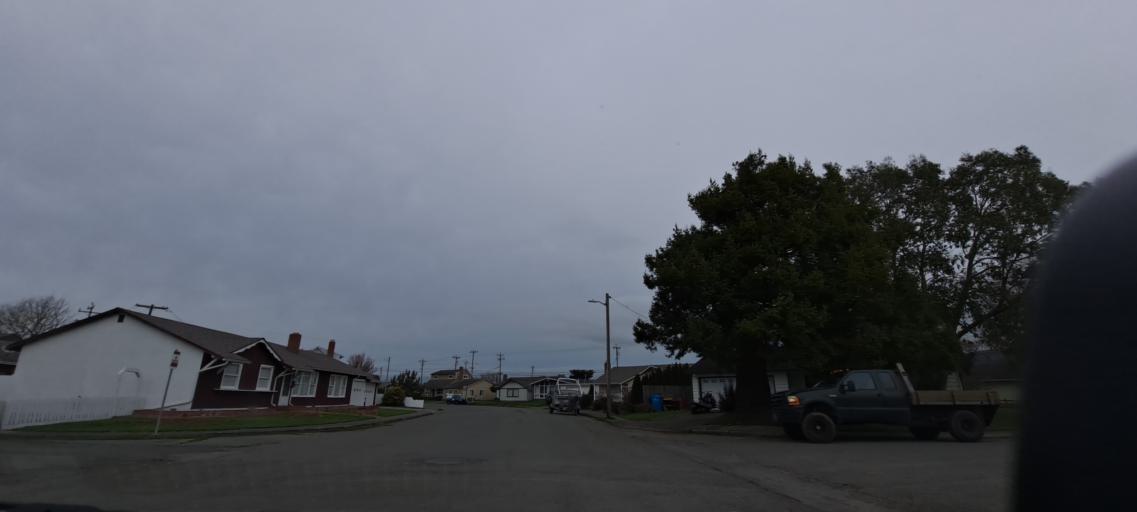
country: US
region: California
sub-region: Humboldt County
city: Arcata
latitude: 40.8727
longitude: -124.1023
